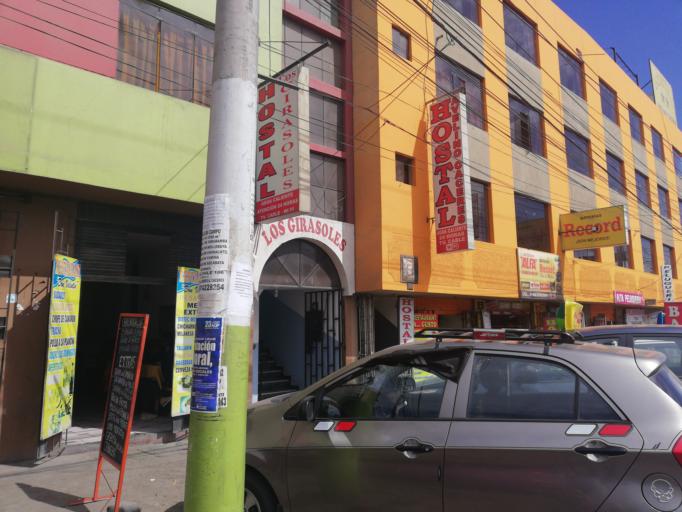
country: PE
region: Arequipa
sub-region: Provincia de Arequipa
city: Arequipa
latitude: -16.4233
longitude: -71.5412
